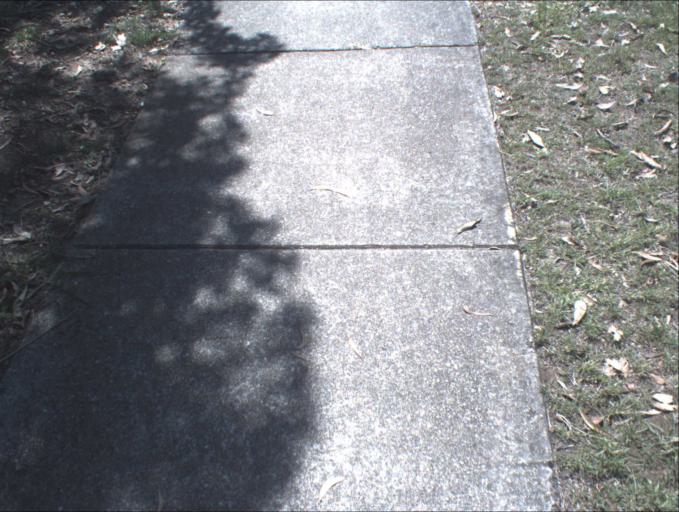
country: AU
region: Queensland
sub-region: Logan
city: Beenleigh
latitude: -27.7022
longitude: 153.1735
